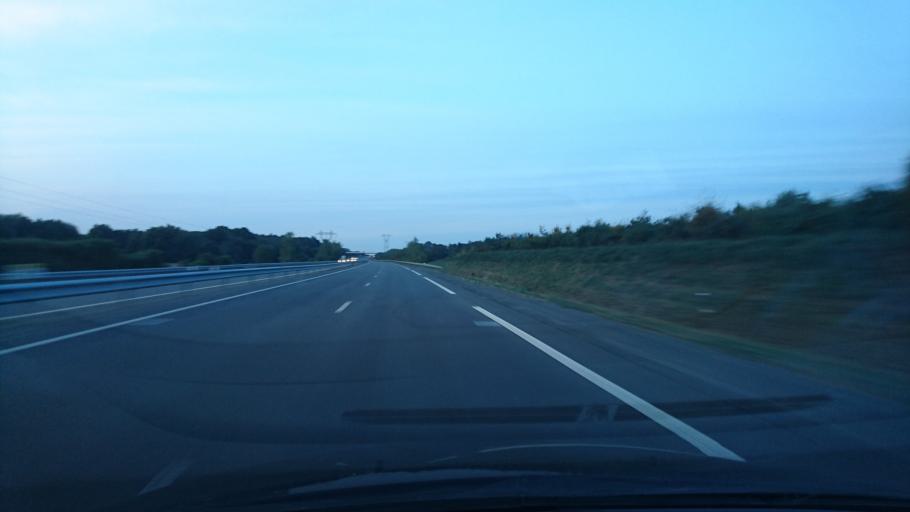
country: FR
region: Brittany
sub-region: Departement d'Ille-et-Vilaine
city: Guichen
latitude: 47.9842
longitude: -1.8136
